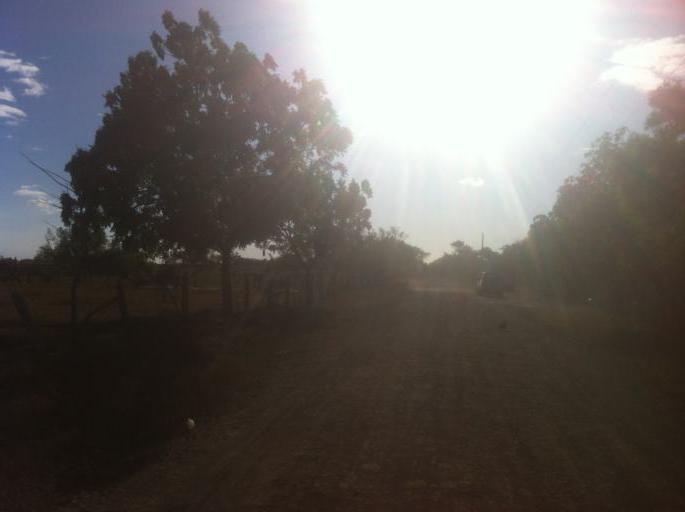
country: NI
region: Managua
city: Carlos Fonseca Amador
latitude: 11.8953
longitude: -86.5866
